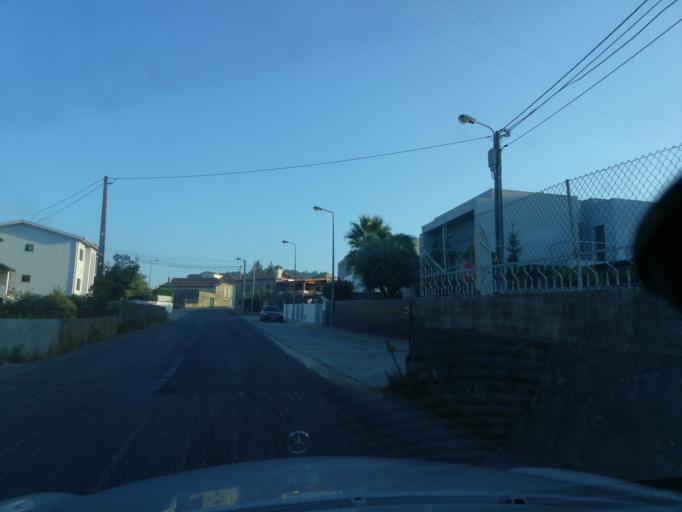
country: PT
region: Braga
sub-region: Braga
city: Braga
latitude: 41.5268
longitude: -8.4280
